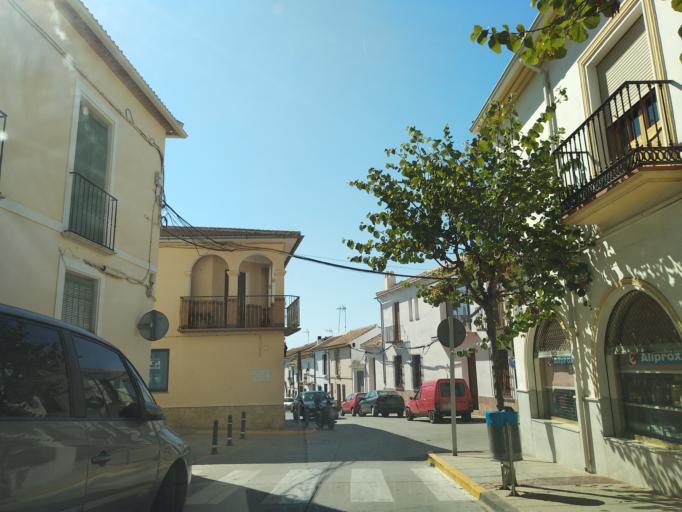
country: ES
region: Andalusia
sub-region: Provincia de Malaga
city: Mollina
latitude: 37.1251
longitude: -4.6570
